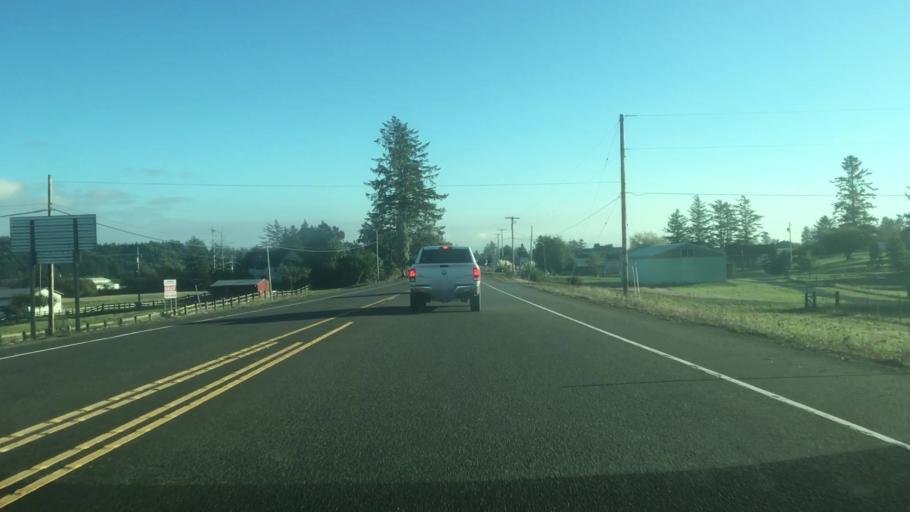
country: US
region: Oregon
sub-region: Clatsop County
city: Warrenton
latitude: 46.1196
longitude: -123.9255
